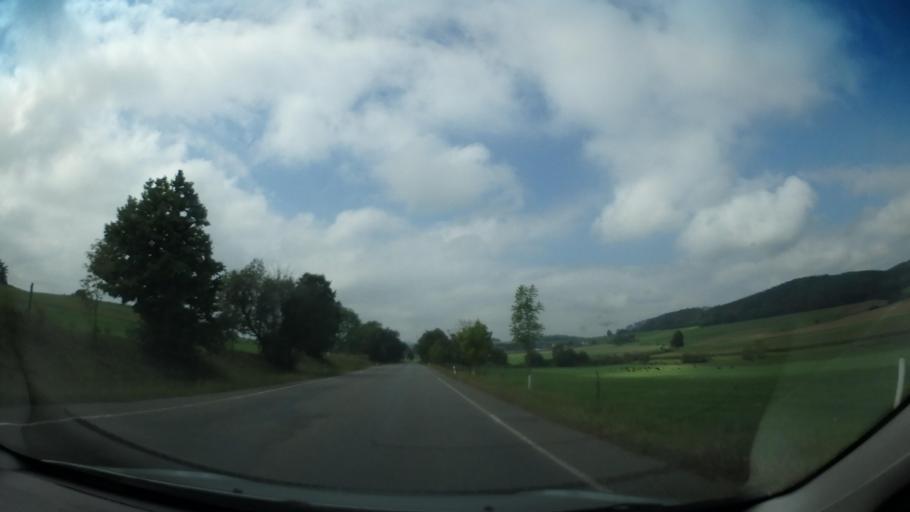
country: CZ
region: Central Bohemia
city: Sedlcany
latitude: 49.7006
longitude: 14.3668
